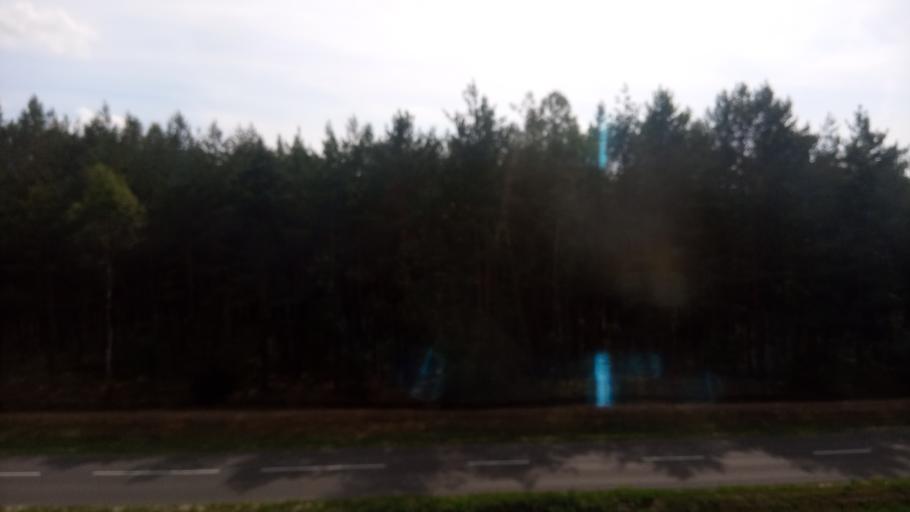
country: PL
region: Greater Poland Voivodeship
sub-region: Powiat pilski
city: Kaczory
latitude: 53.1143
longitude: 16.8380
